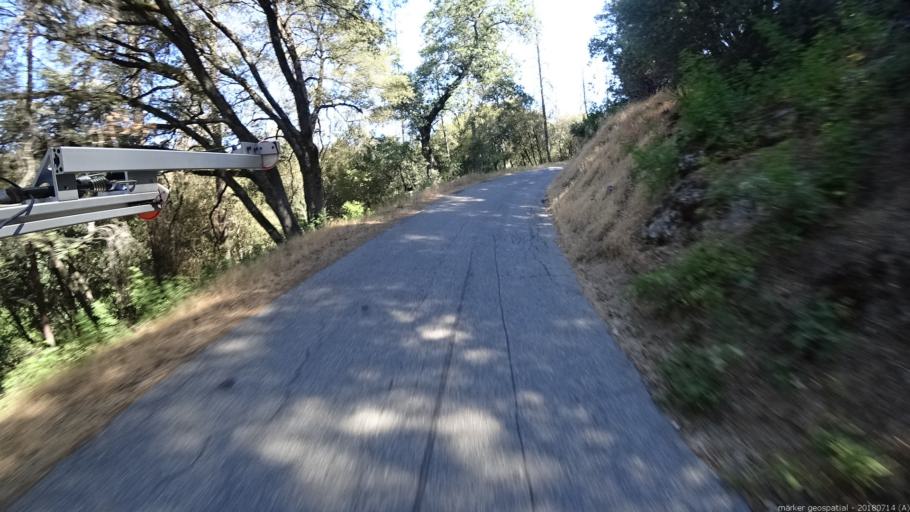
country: US
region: California
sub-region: Madera County
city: Oakhurst
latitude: 37.3714
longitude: -119.6261
